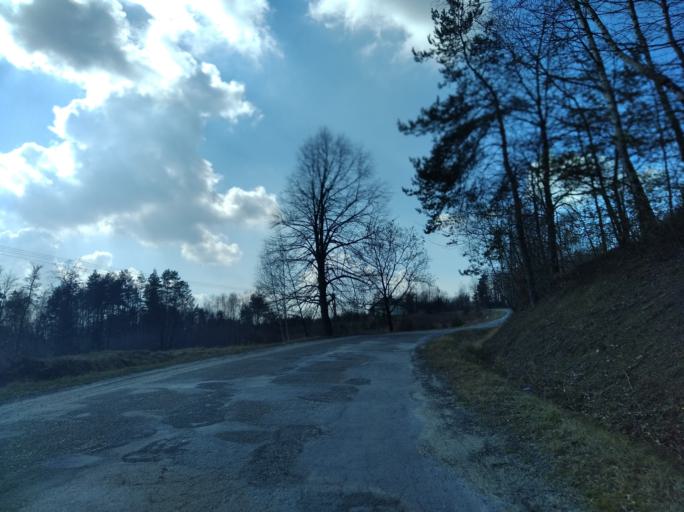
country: PL
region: Subcarpathian Voivodeship
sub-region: Powiat debicki
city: Brzostek
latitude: 49.8920
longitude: 21.4839
